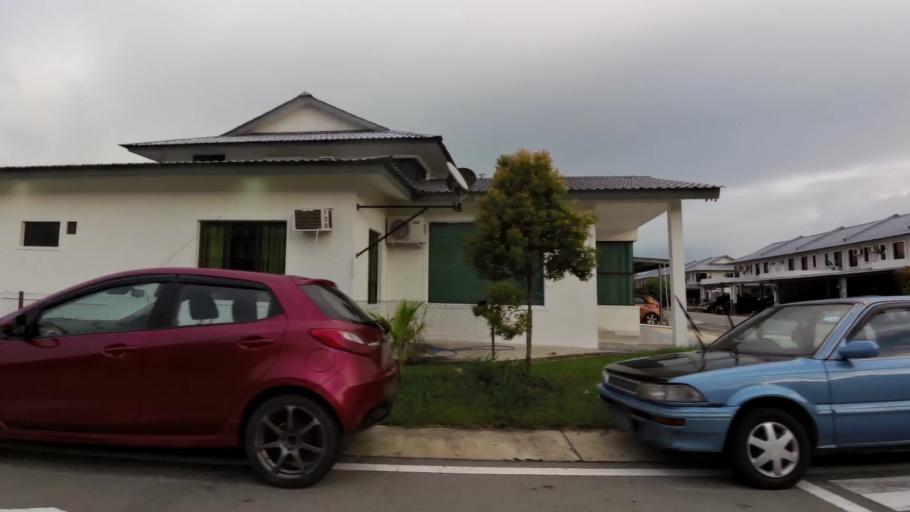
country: BN
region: Brunei and Muara
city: Bandar Seri Begawan
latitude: 4.9967
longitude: 114.9873
